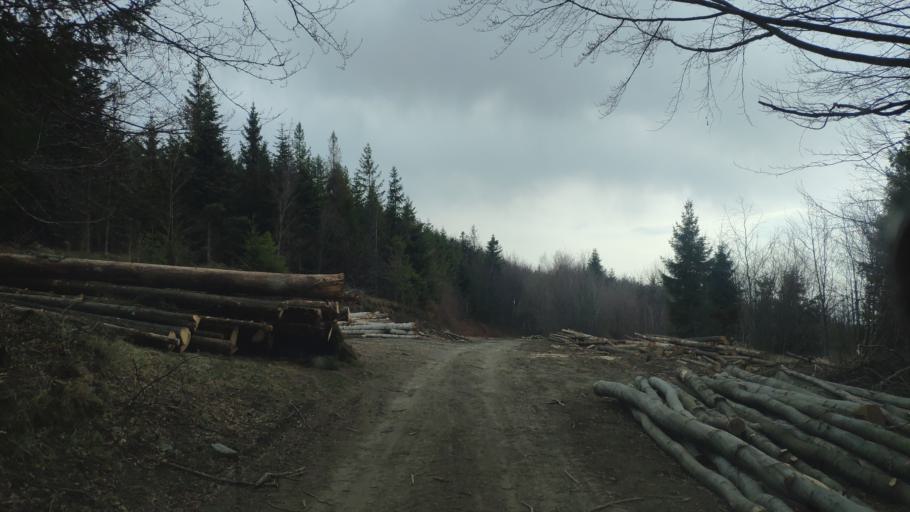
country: SK
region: Kosicky
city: Moldava nad Bodvou
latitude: 48.7519
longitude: 21.0419
